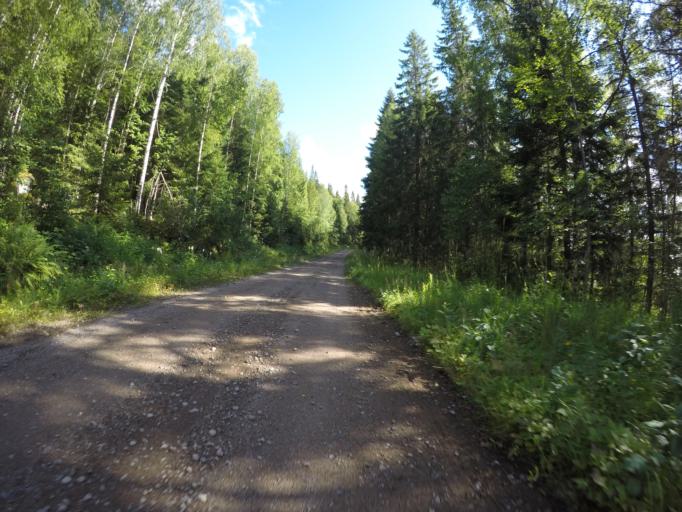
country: SE
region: OErebro
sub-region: Hallefors Kommun
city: Haellefors
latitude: 59.9918
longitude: 14.6070
